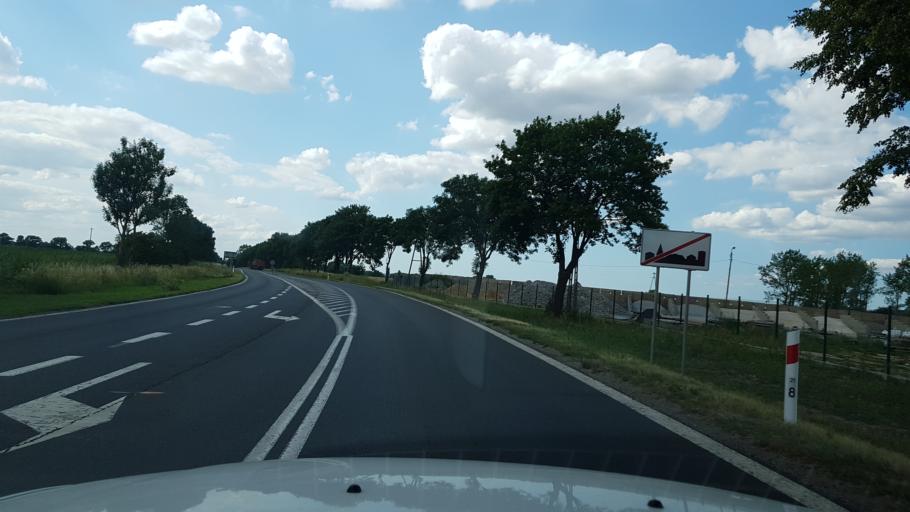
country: PL
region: West Pomeranian Voivodeship
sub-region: Powiat pyrzycki
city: Pyrzyce
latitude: 53.1895
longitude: 14.8379
